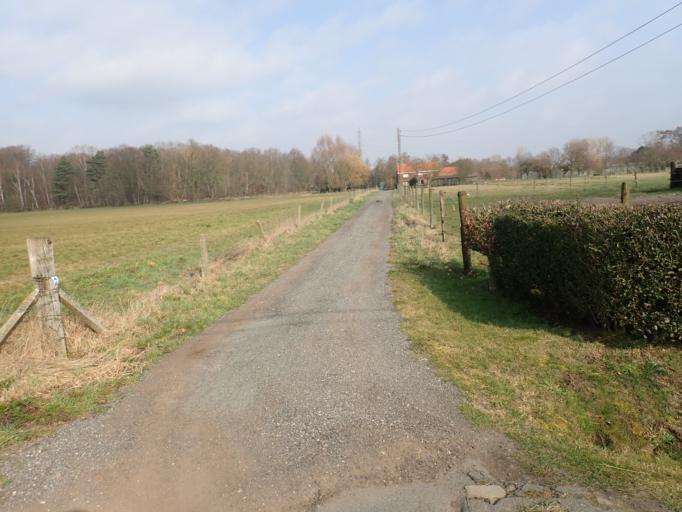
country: BE
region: Flanders
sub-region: Provincie Antwerpen
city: Heist-op-den-Berg
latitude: 51.0593
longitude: 4.6933
